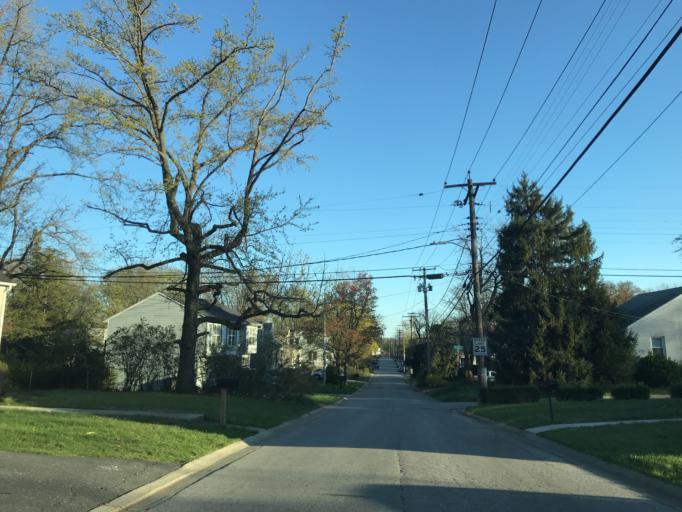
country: US
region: Maryland
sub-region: Baltimore County
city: Overlea
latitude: 39.3406
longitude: -76.5348
